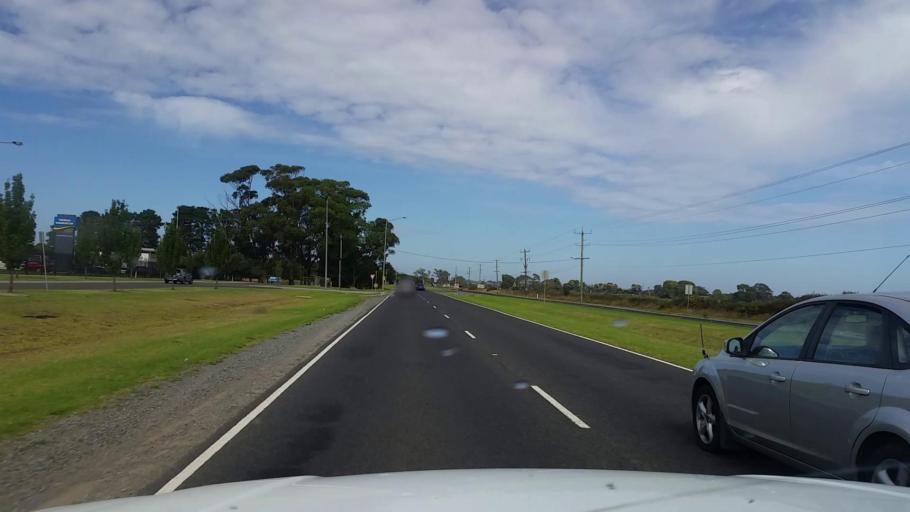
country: AU
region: Victoria
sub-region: Frankston
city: Sandhurst
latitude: -38.0519
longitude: 145.2081
